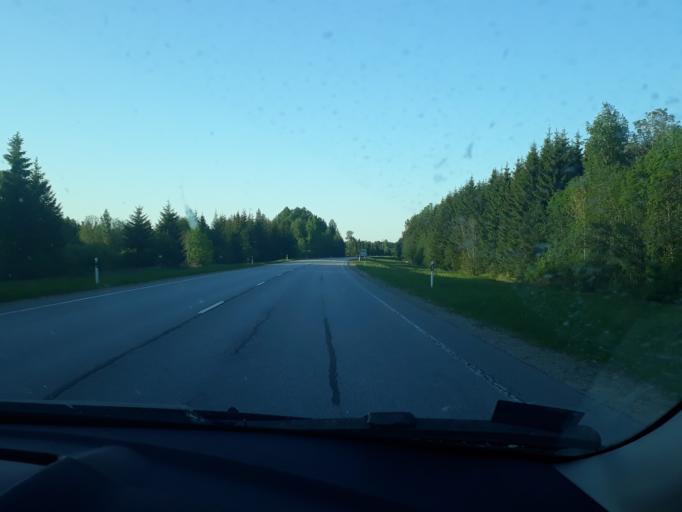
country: EE
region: Paernumaa
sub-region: Sindi linn
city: Sindi
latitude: 58.4611
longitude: 24.7001
